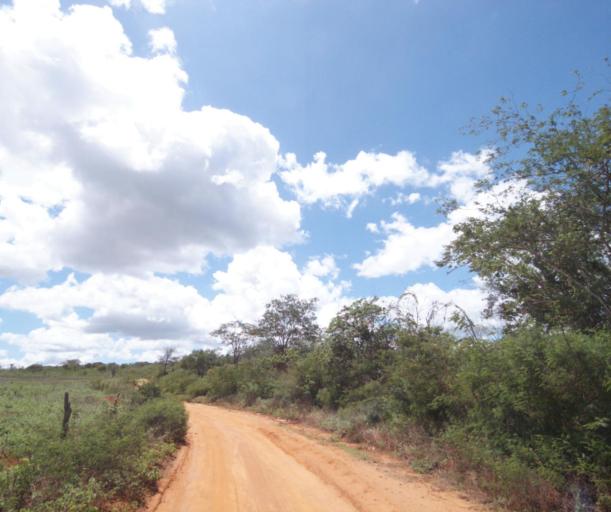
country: BR
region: Bahia
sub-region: Pocoes
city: Pocoes
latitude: -14.3898
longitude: -40.5291
